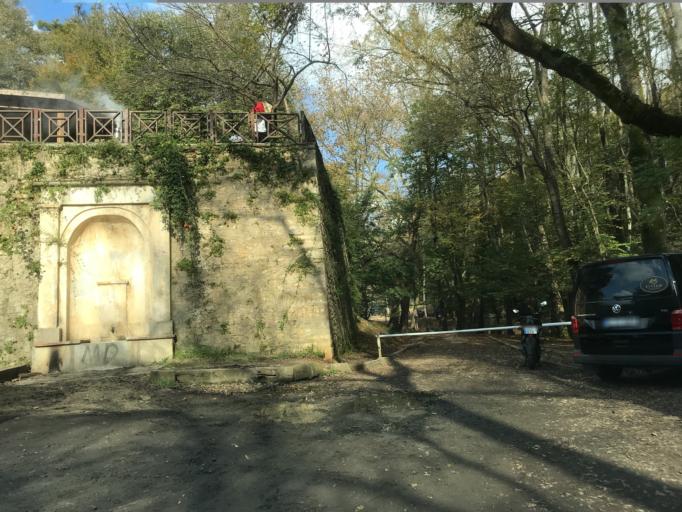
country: TR
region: Istanbul
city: Arikoey
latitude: 41.1893
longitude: 28.9870
